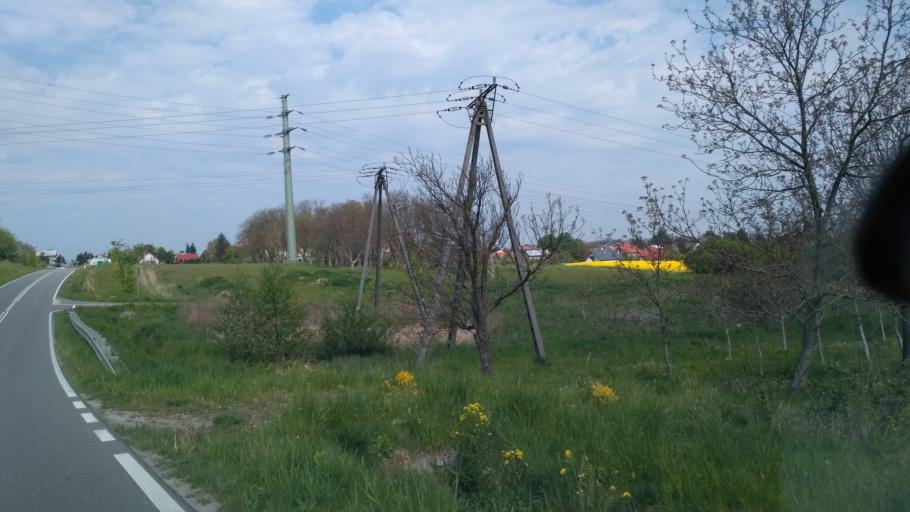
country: PL
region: Subcarpathian Voivodeship
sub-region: Powiat jaroslawski
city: Jaroslaw
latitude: 49.9985
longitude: 22.6765
